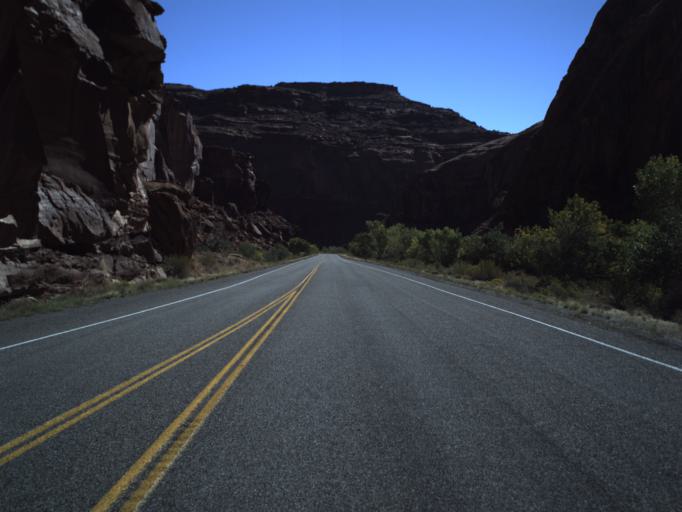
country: US
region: Utah
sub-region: San Juan County
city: Blanding
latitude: 37.9624
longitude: -110.4895
